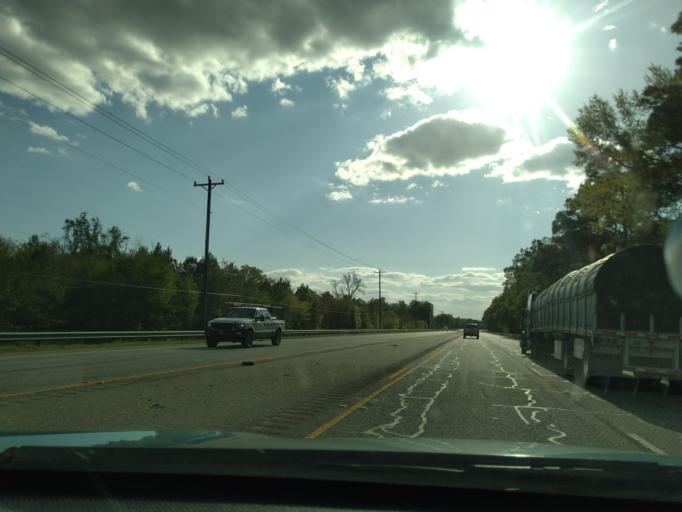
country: US
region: South Carolina
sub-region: Williamsburg County
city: Kingstree
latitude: 33.6598
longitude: -79.8467
